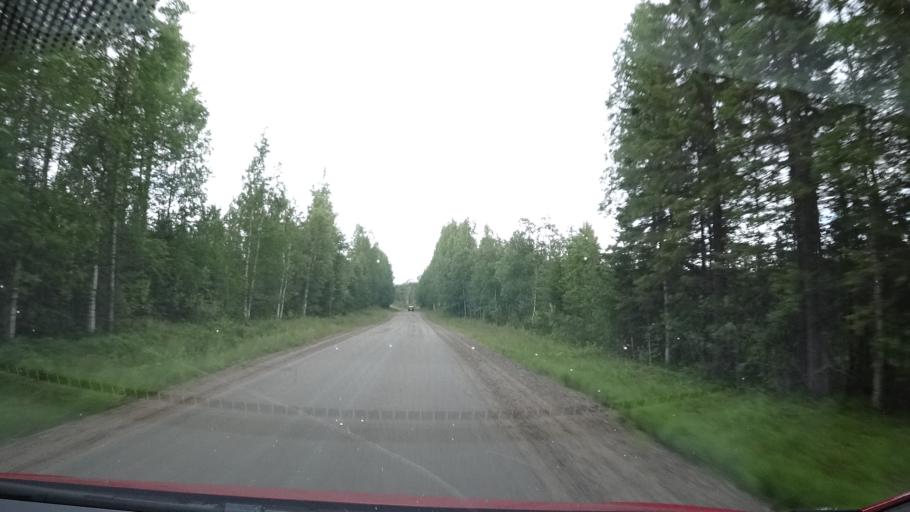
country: FI
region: Kainuu
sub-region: Kehys-Kainuu
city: Kuhmo
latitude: 63.9430
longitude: 29.2134
